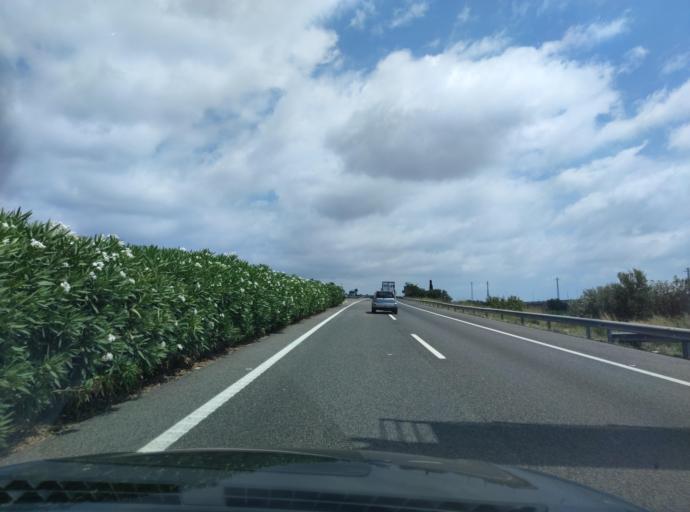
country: ES
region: Catalonia
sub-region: Provincia de Tarragona
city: Amposta
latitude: 40.7505
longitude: 0.5980
